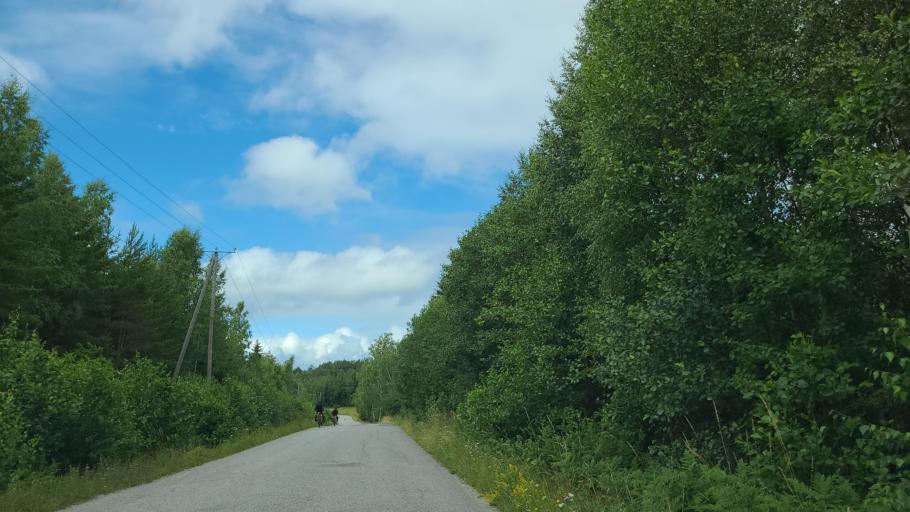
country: FI
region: Varsinais-Suomi
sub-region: Aboland-Turunmaa
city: Nagu
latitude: 60.1712
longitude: 21.9808
